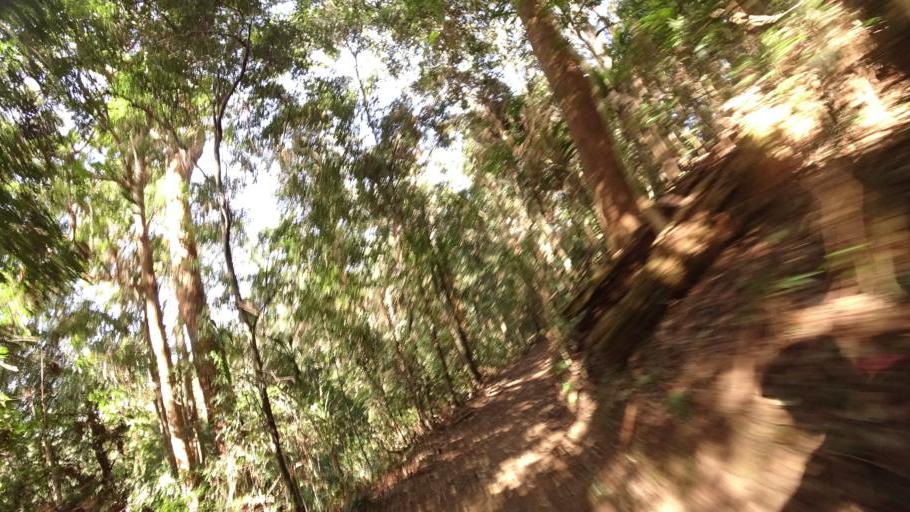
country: AU
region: Queensland
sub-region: Moreton Bay
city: Highvale
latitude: -27.4019
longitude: 152.7941
